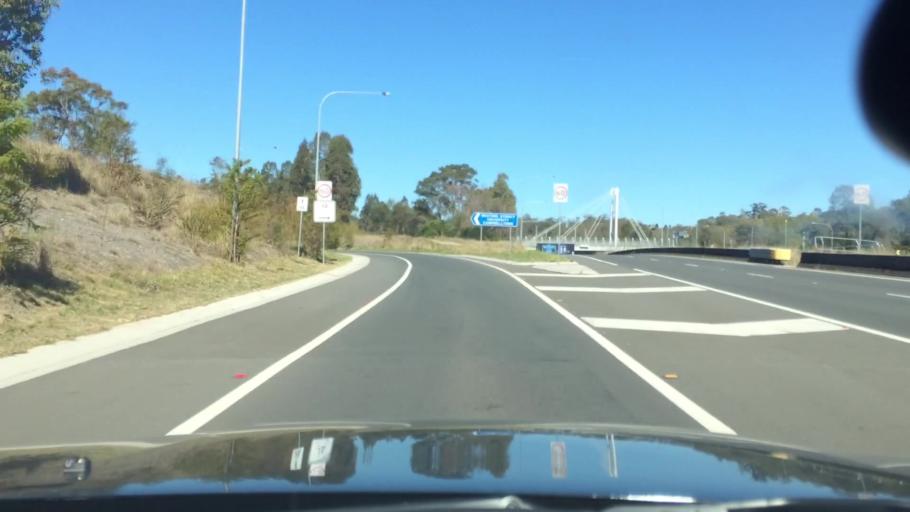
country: AU
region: New South Wales
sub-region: Campbelltown Municipality
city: Glen Alpine
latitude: -34.0605
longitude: 150.7882
